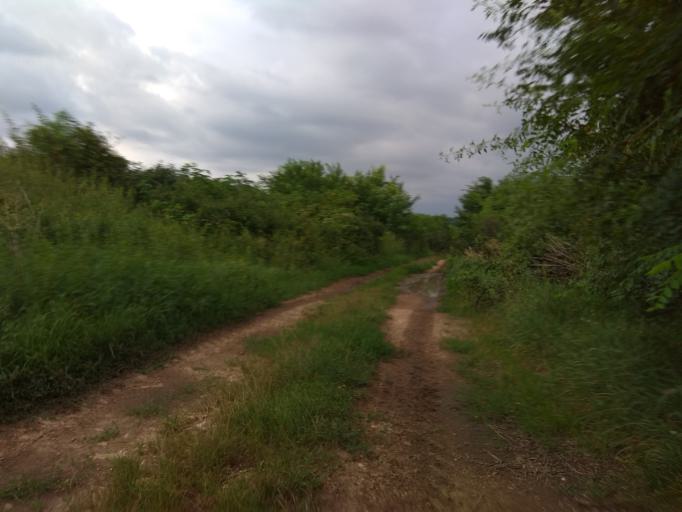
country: HU
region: Borsod-Abauj-Zemplen
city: Monok
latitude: 48.1779
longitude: 21.1232
